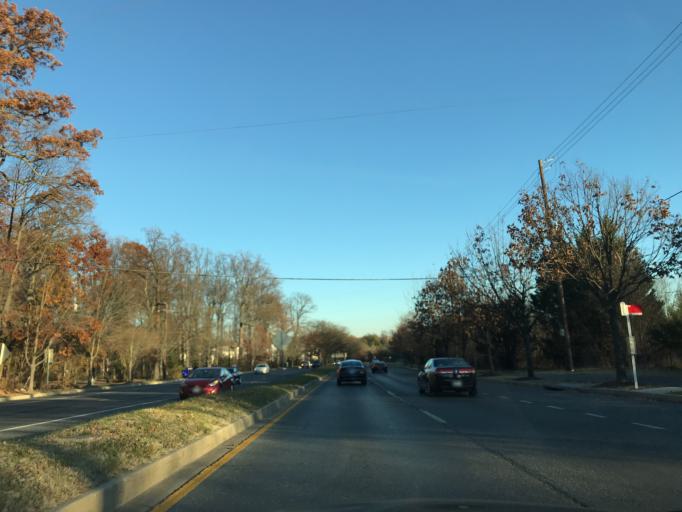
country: US
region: Maryland
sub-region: Montgomery County
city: Olney
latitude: 39.1496
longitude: -77.0580
